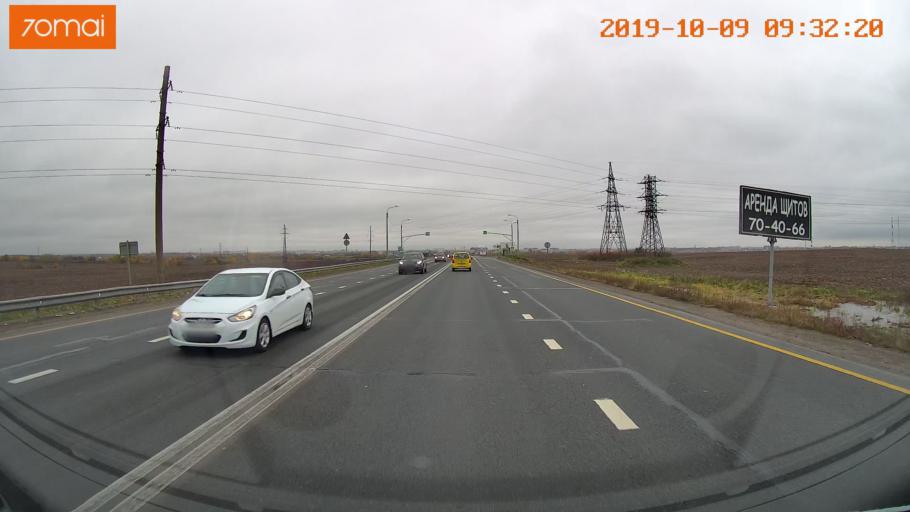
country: RU
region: Vologda
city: Vologda
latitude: 59.1577
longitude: 39.9296
